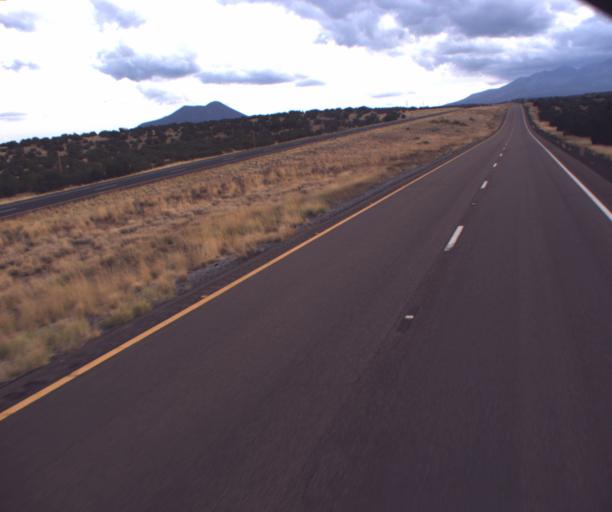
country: US
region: Arizona
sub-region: Coconino County
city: Flagstaff
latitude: 35.5072
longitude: -111.5484
